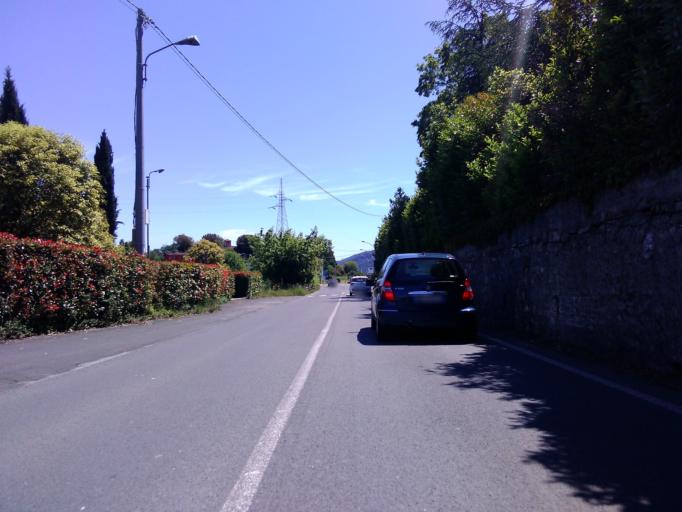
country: IT
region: Liguria
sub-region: Provincia di La Spezia
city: Sarzana
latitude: 44.1225
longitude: 9.9438
